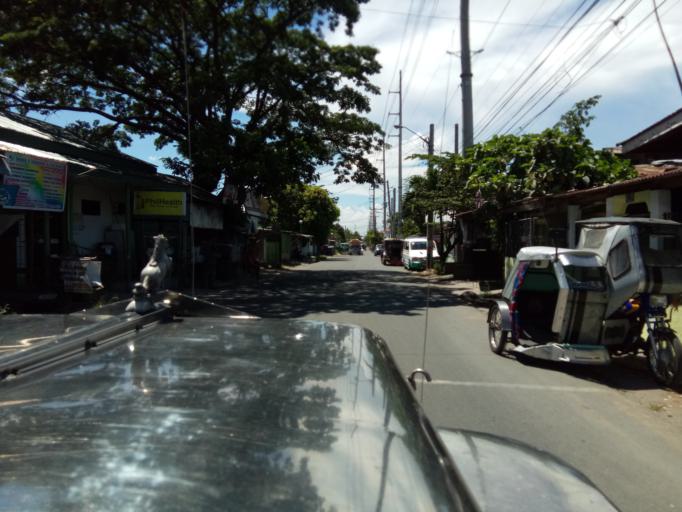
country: PH
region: Calabarzon
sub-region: Province of Cavite
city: Pasong Kawayan Primero
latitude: 14.3581
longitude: 120.8979
